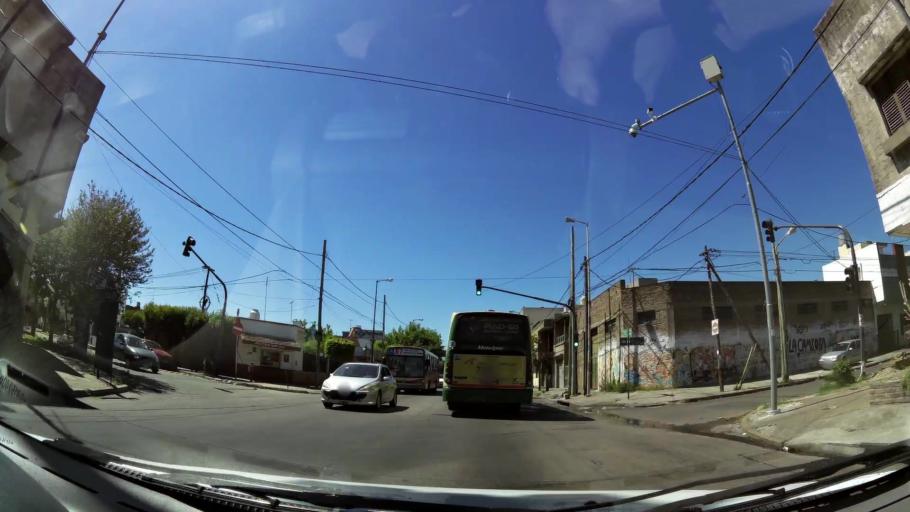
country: AR
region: Buenos Aires
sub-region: Partido de General San Martin
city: General San Martin
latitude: -34.5420
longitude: -58.5403
